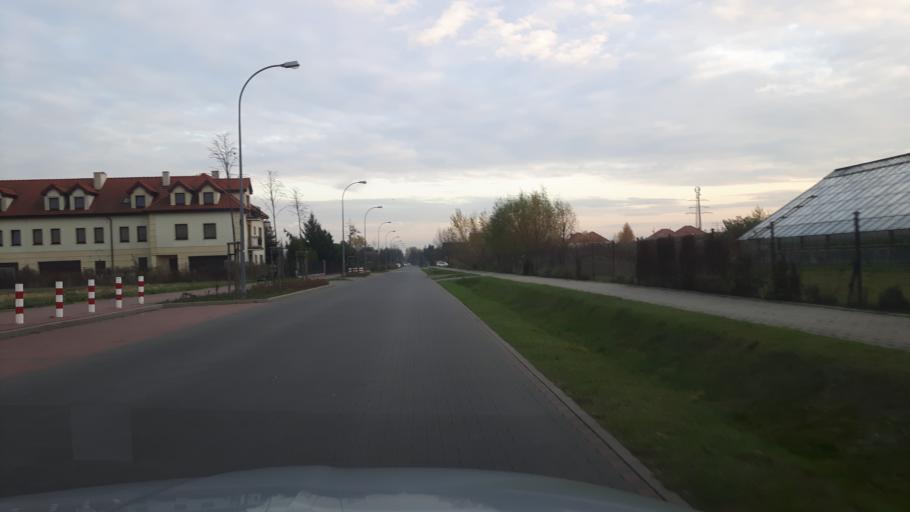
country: PL
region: Masovian Voivodeship
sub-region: Warszawa
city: Wilanow
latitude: 52.1777
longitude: 21.1084
